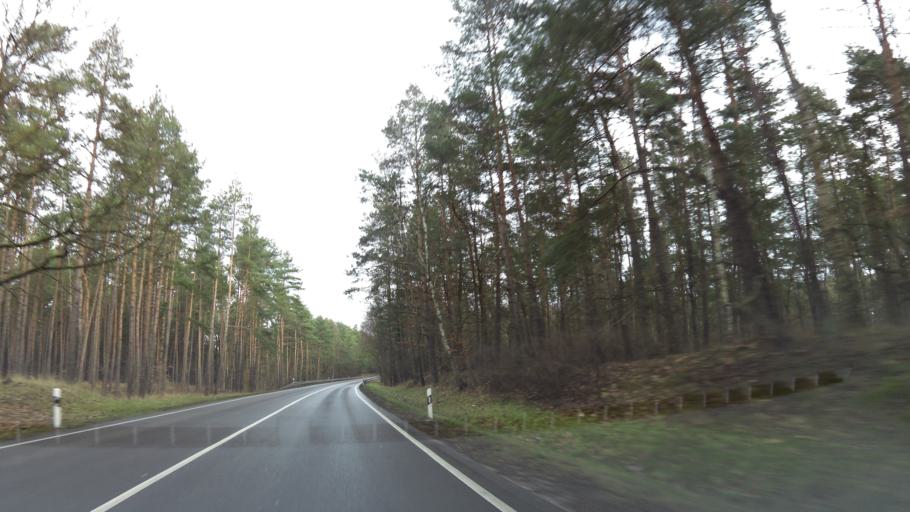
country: DE
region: Brandenburg
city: Strausberg
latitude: 52.5888
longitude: 13.8718
